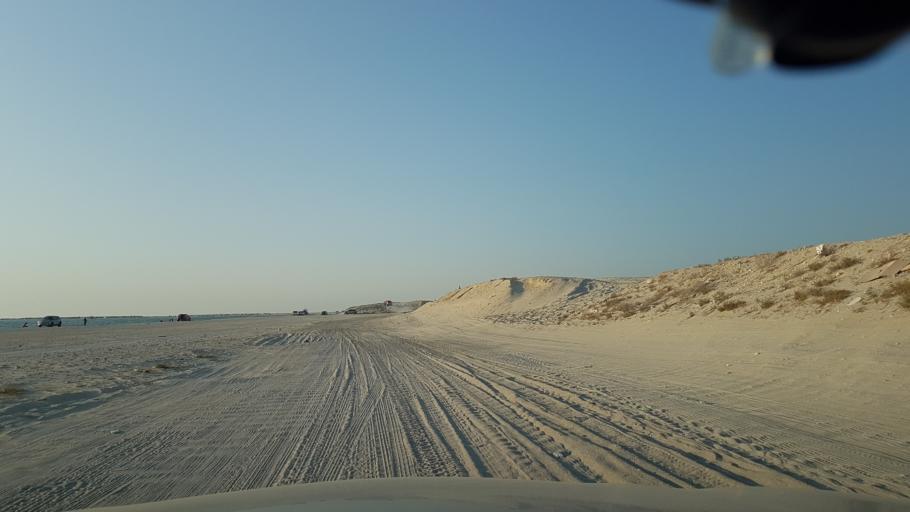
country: BH
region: Manama
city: Jidd Hafs
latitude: 26.2437
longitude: 50.5031
